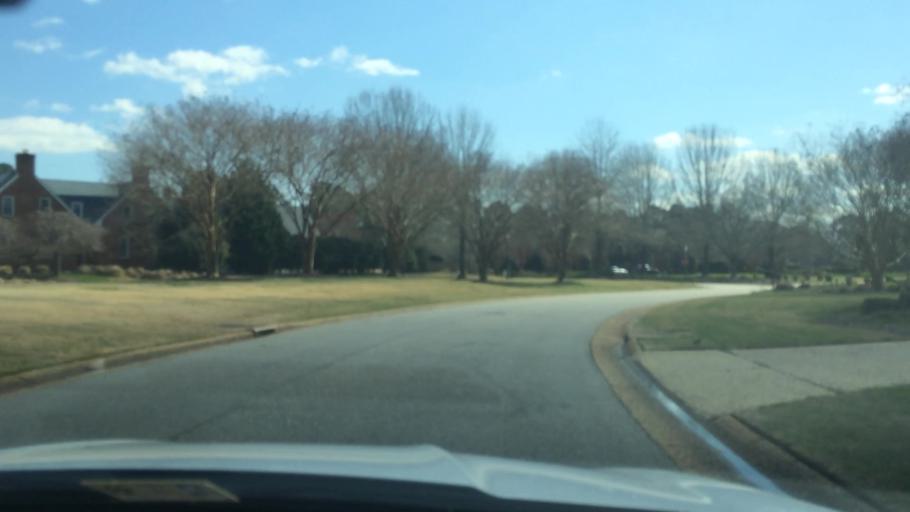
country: US
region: Virginia
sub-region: City of Williamsburg
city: Williamsburg
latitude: 37.2280
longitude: -76.6786
